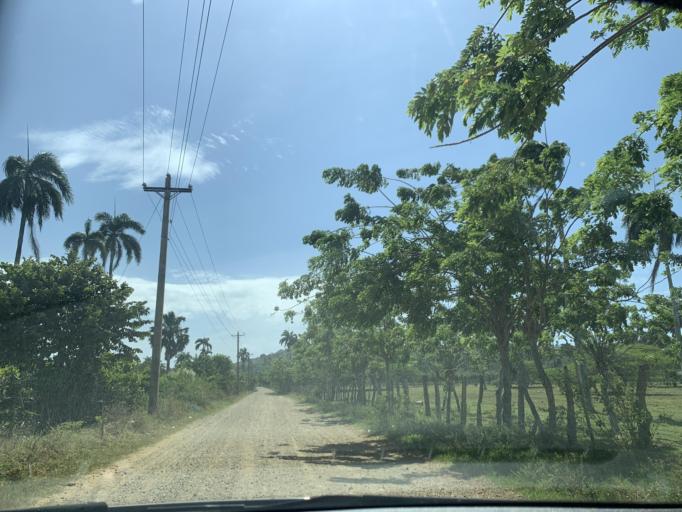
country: DO
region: Puerto Plata
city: Luperon
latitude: 19.8900
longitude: -70.8802
